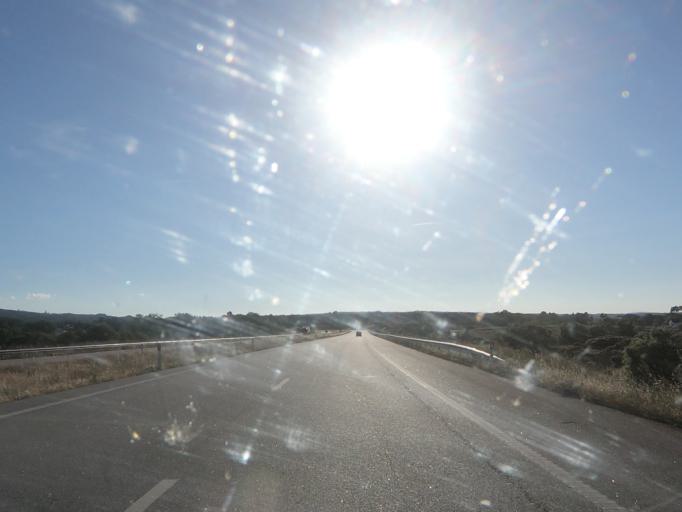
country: PT
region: Guarda
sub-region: Guarda
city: Sequeira
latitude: 40.6017
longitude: -7.0957
